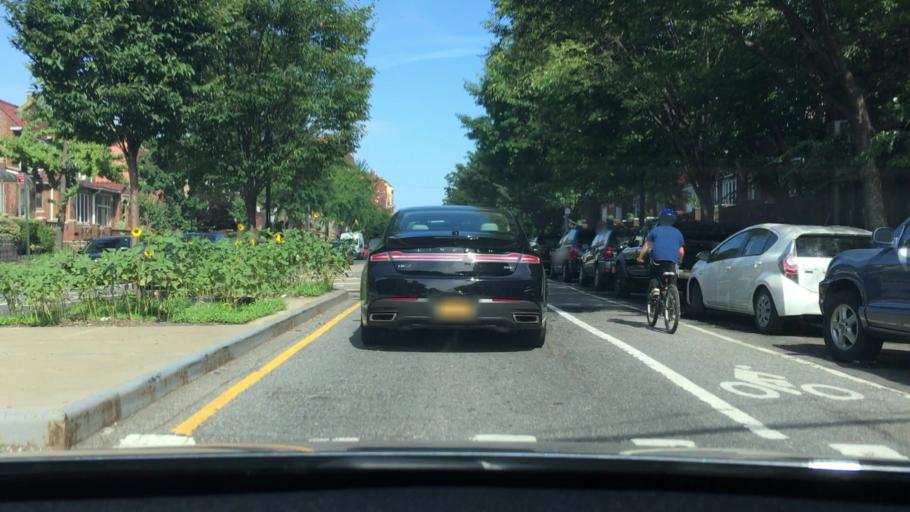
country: US
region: New York
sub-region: Kings County
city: Brooklyn
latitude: 40.6640
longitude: -73.9426
